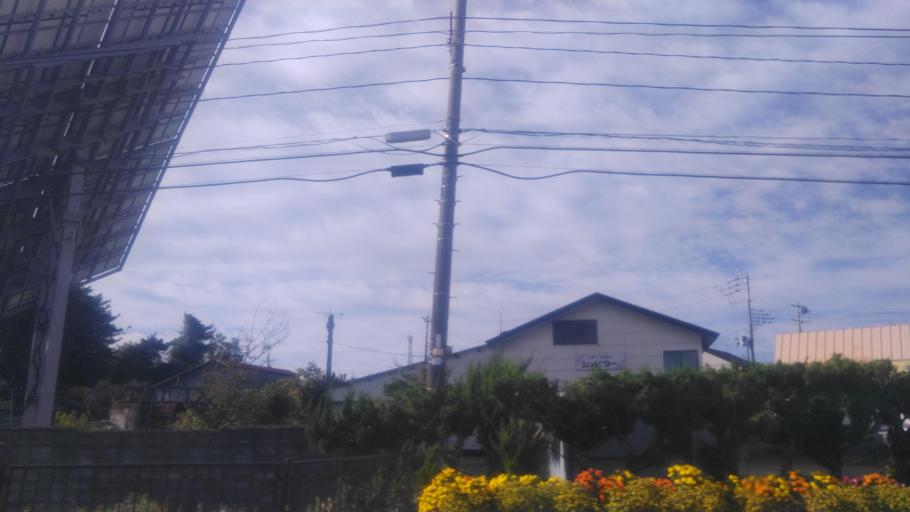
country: JP
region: Akita
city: Noshiromachi
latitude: 40.1862
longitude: 140.0457
